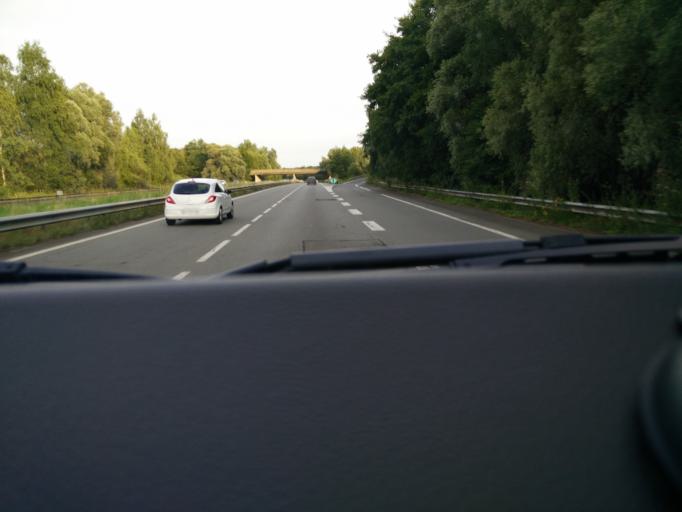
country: FR
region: Nord-Pas-de-Calais
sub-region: Departement du Nord
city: Hasnon
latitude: 50.4214
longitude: 3.4040
